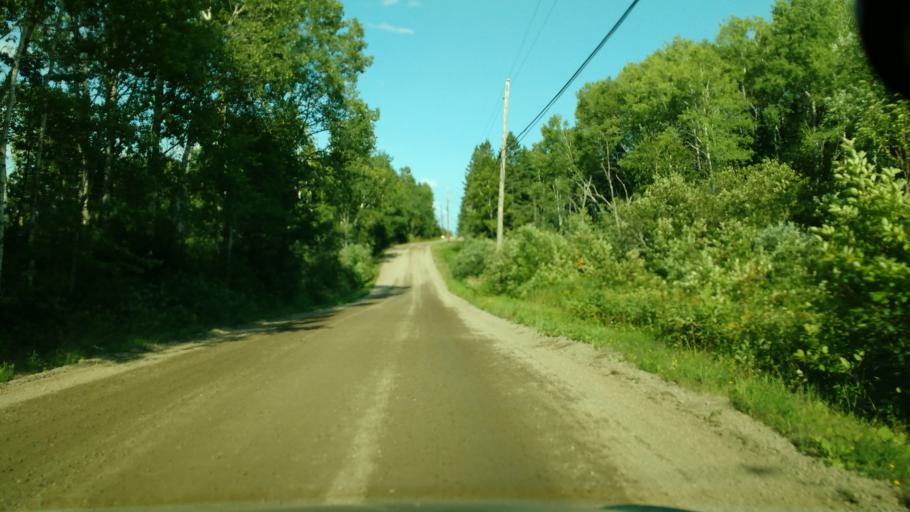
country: CA
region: Ontario
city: Powassan
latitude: 46.1828
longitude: -79.2938
